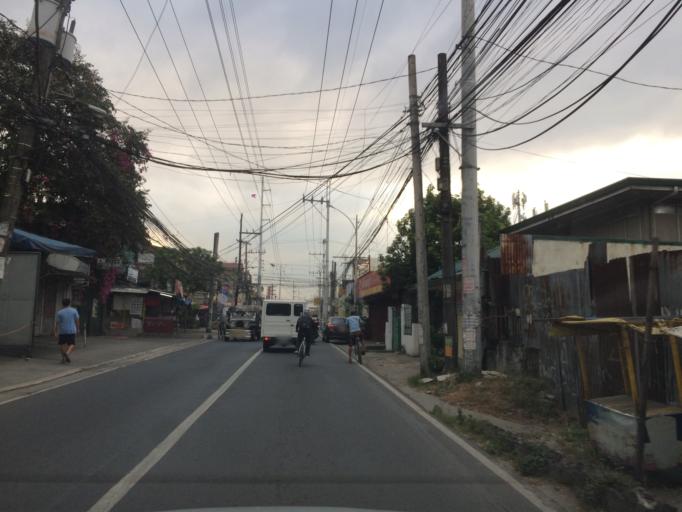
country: PH
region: Calabarzon
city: Bagong Pagasa
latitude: 14.6767
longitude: 121.0408
